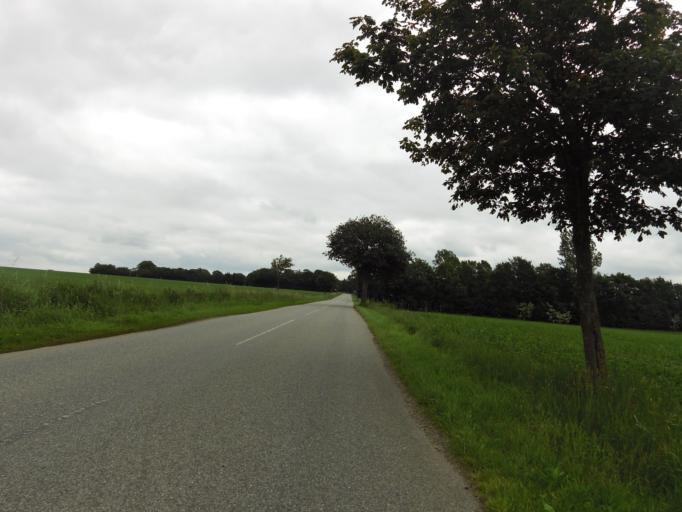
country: DK
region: South Denmark
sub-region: Tonder Kommune
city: Toftlund
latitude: 55.1023
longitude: 9.0949
